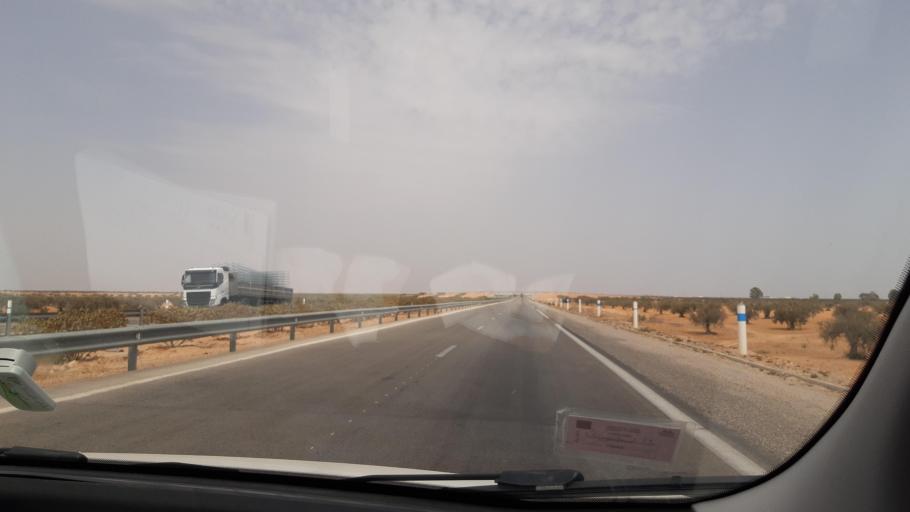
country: TN
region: Safaqis
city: Bi'r `Ali Bin Khalifah
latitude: 34.5834
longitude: 10.4050
